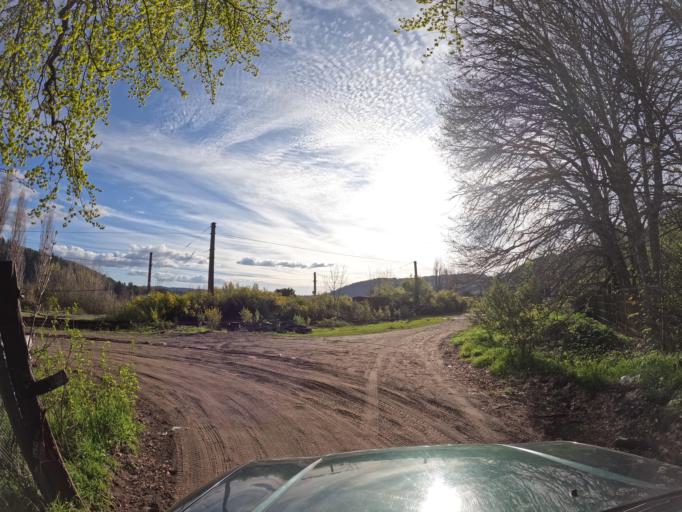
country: CL
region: Biobio
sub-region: Provincia de Biobio
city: La Laja
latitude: -37.2020
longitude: -72.7708
